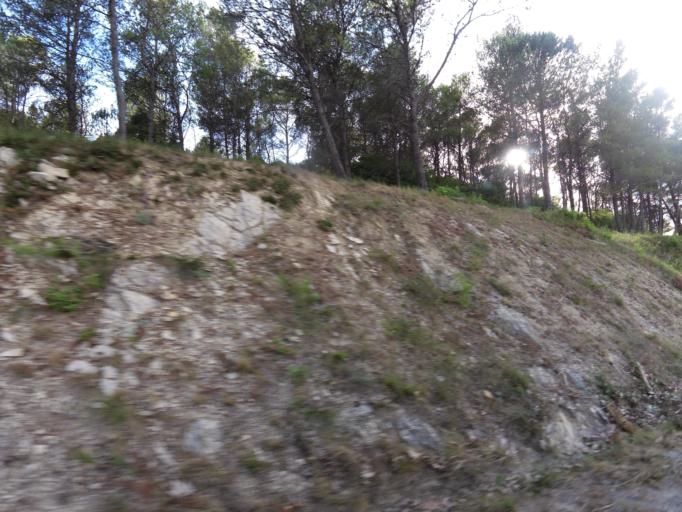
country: FR
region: Languedoc-Roussillon
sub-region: Departement du Gard
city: Congenies
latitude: 43.8006
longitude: 4.1590
